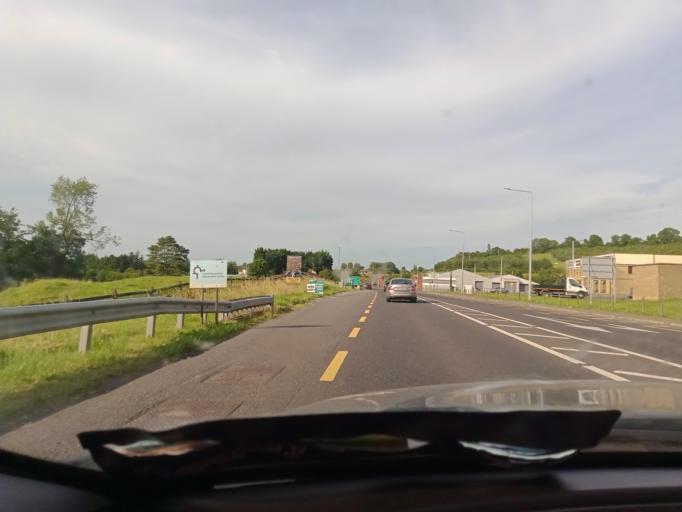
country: IE
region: Ulster
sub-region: An Cabhan
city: Cavan
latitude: 53.9627
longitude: -7.3590
